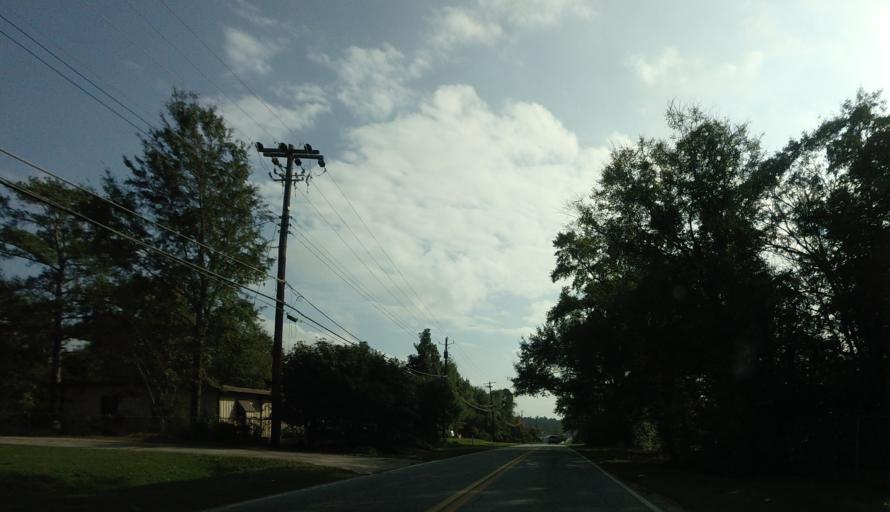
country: US
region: Georgia
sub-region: Bibb County
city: Macon
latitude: 32.8038
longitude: -83.6651
